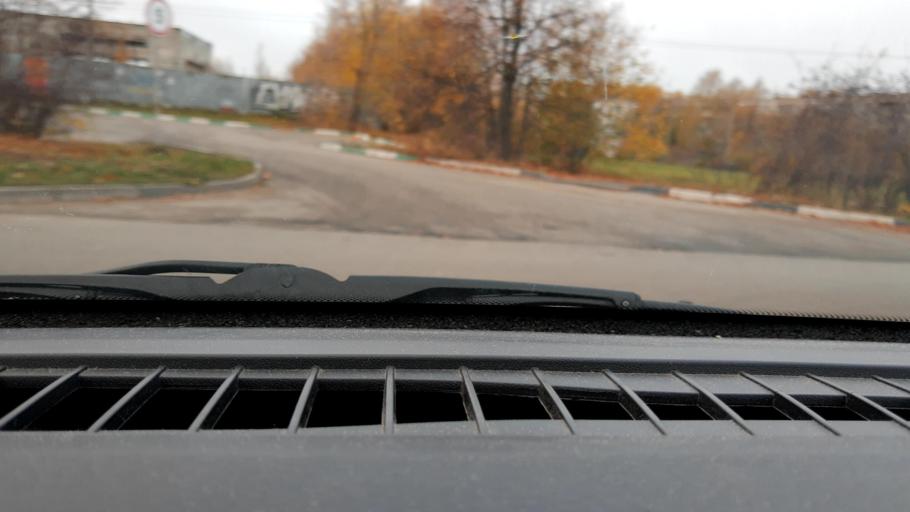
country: RU
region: Nizjnij Novgorod
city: Nizhniy Novgorod
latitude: 56.2578
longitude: 43.9259
